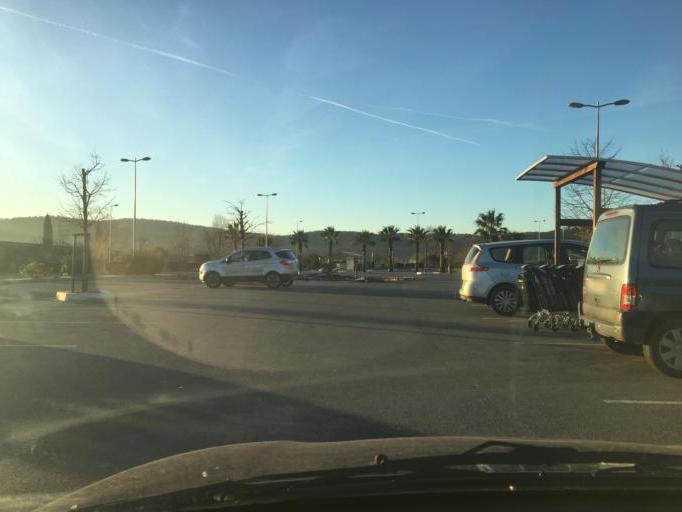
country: FR
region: Provence-Alpes-Cote d'Azur
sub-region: Departement du Var
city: Les Arcs
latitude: 43.4512
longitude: 6.4911
